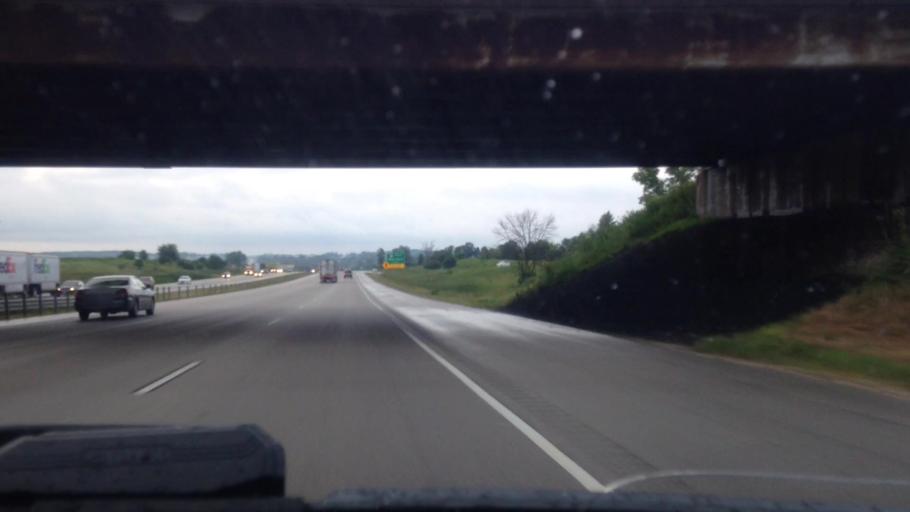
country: US
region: Wisconsin
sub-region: Washington County
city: Richfield
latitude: 43.2504
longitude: -88.1816
